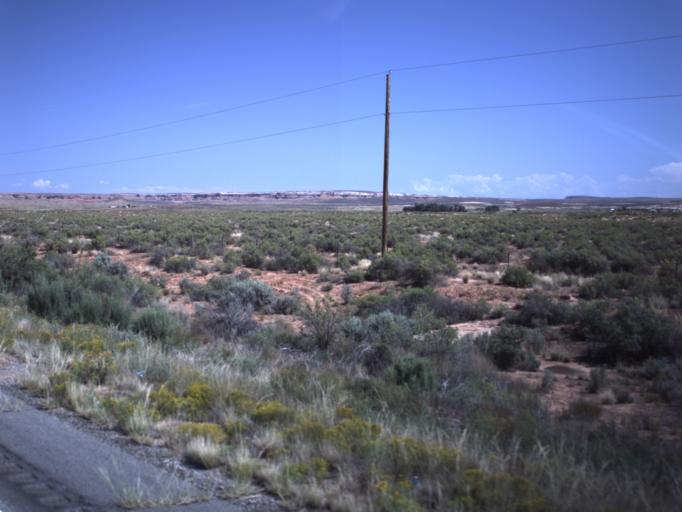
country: US
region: Utah
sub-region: San Juan County
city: Blanding
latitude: 37.1014
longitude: -109.5471
